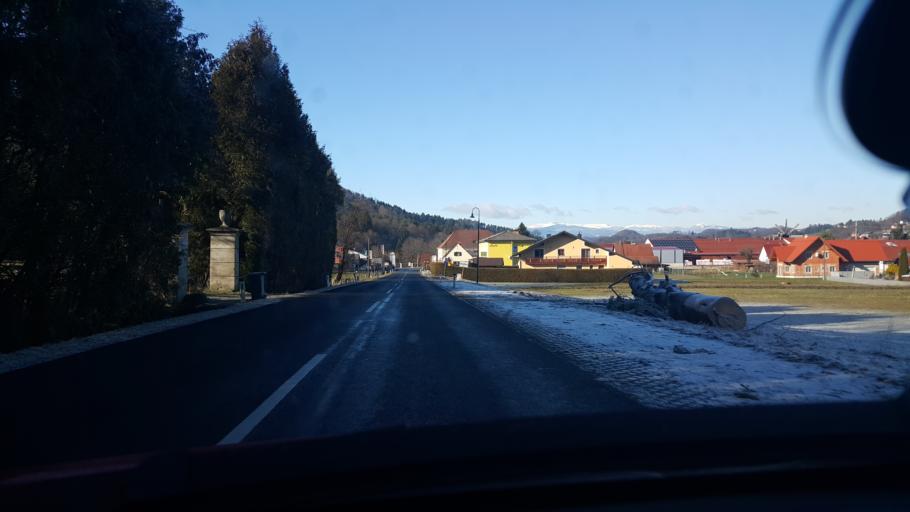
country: AT
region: Styria
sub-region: Politischer Bezirk Leibnitz
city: Leutschach
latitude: 46.6605
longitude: 15.4734
